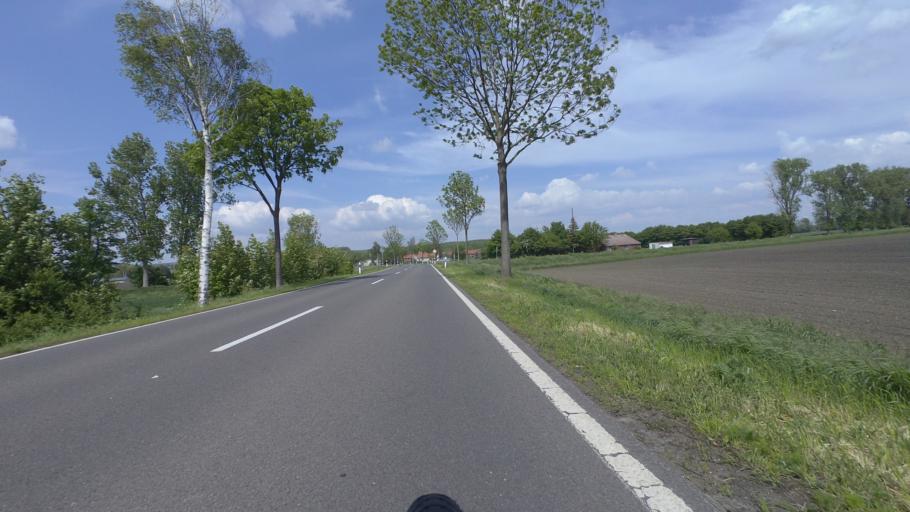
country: DE
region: Lower Saxony
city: Jerxheim
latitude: 52.0616
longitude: 10.8898
